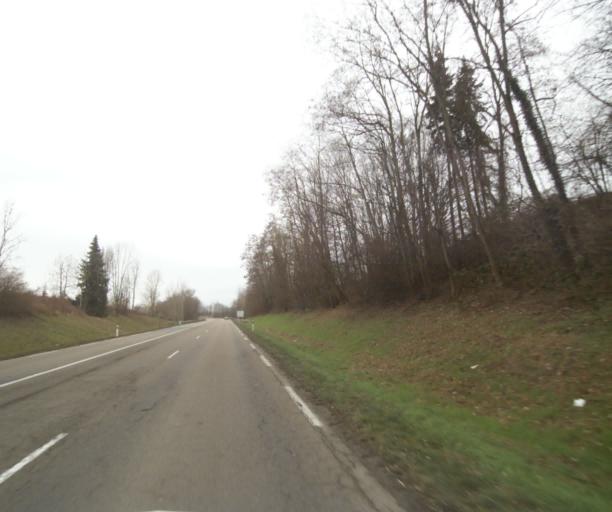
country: FR
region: Champagne-Ardenne
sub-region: Departement de la Haute-Marne
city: Bienville
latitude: 48.5881
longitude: 5.0297
